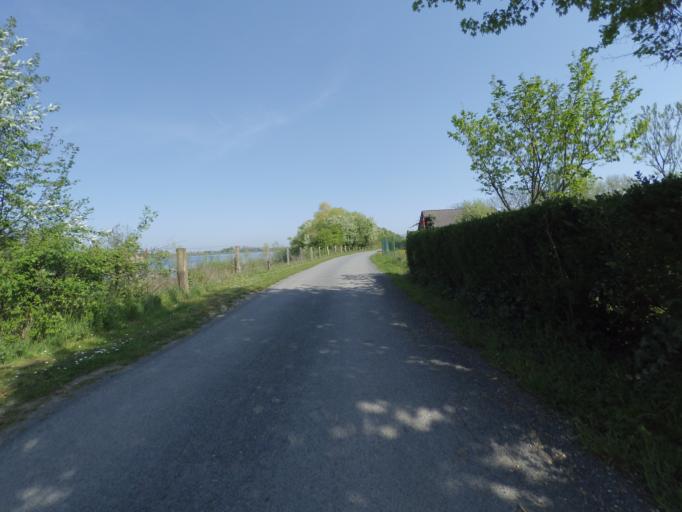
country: DE
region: North Rhine-Westphalia
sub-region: Regierungsbezirk Dusseldorf
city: Mehrhoog
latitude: 51.7099
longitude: 6.4771
